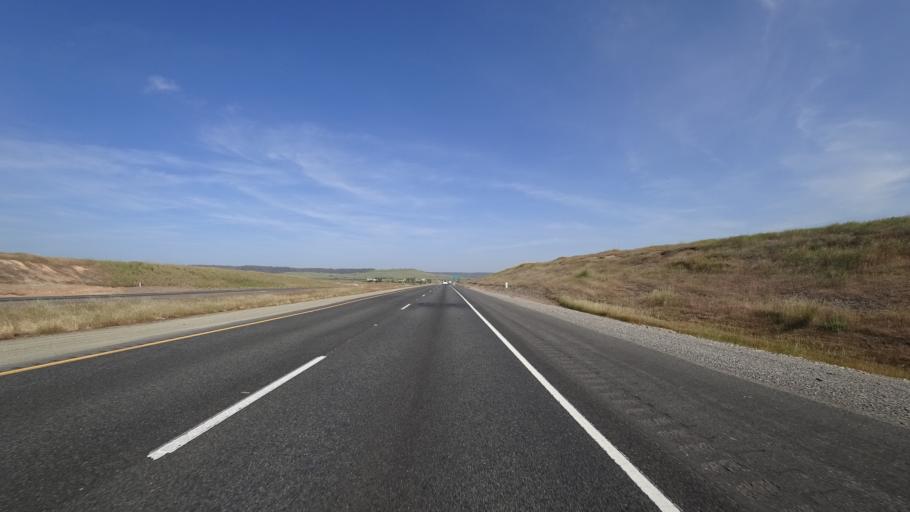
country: US
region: California
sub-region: Butte County
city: Thermalito
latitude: 39.5954
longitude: -121.6497
